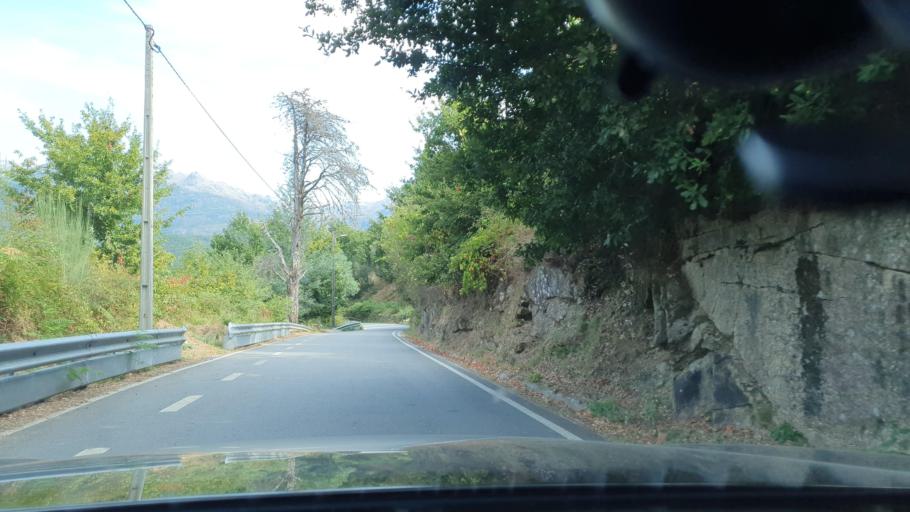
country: PT
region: Braga
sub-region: Vieira do Minho
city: Vieira do Minho
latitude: 41.6828
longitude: -8.0994
